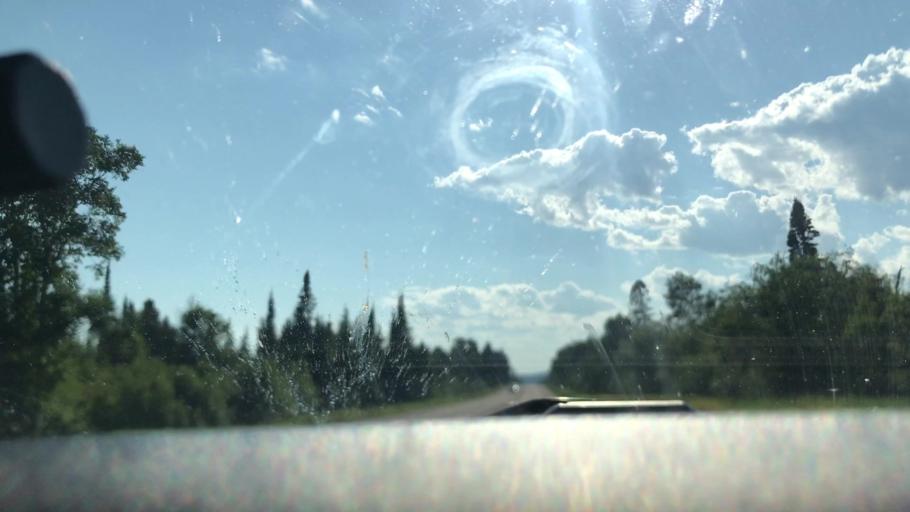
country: US
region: Minnesota
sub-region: Cook County
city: Grand Marais
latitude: 47.7969
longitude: -90.1195
